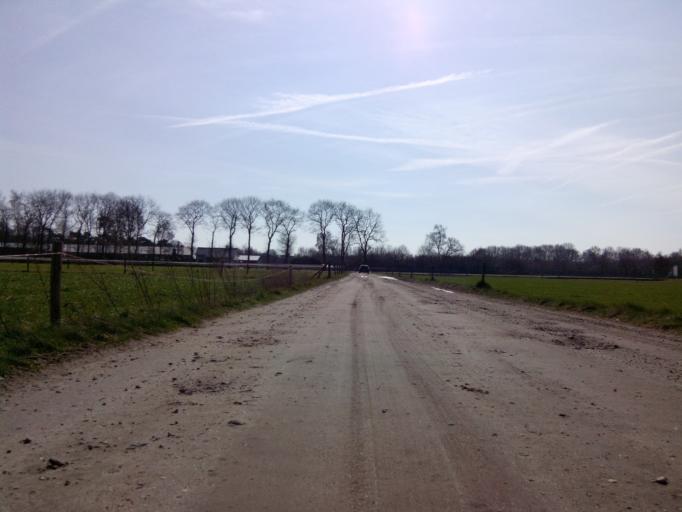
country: NL
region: Gelderland
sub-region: Gemeente Barneveld
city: Voorthuizen
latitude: 52.2073
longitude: 5.6396
